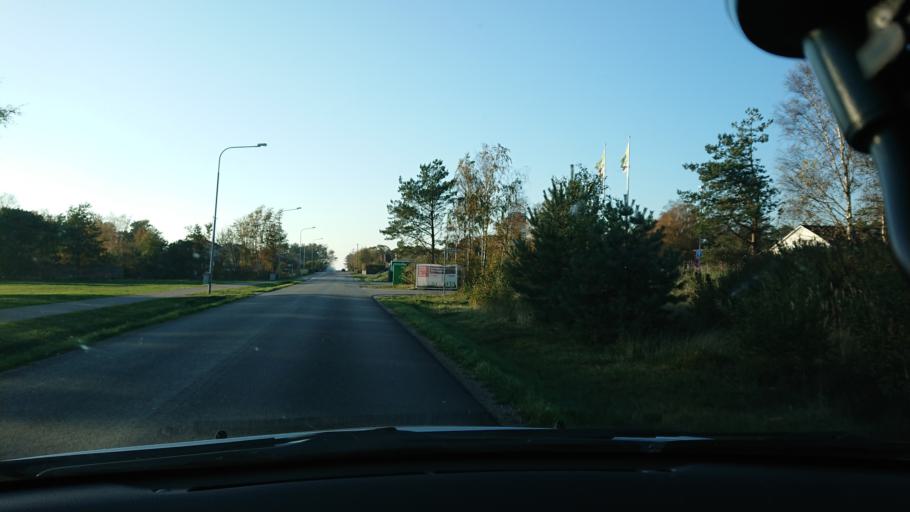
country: SE
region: Halland
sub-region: Laholms Kommun
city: Mellbystrand
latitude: 56.4598
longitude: 12.9273
